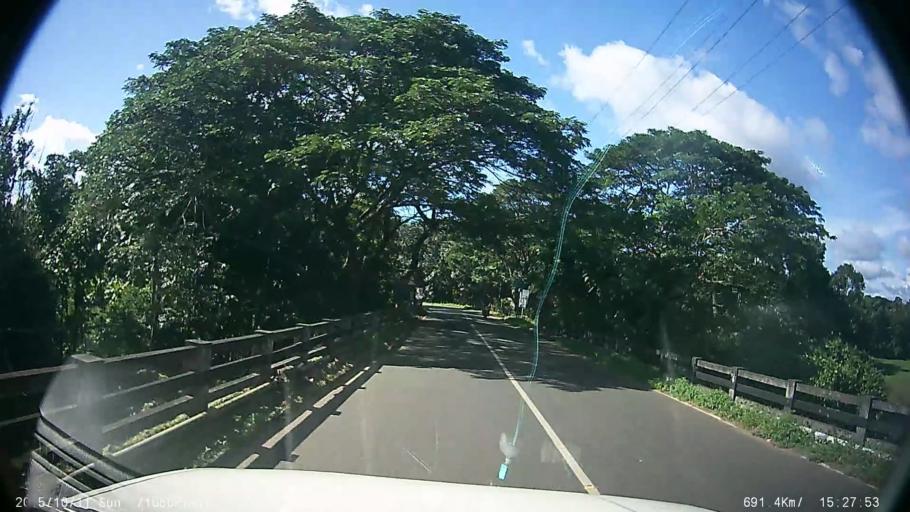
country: IN
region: Kerala
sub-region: Kottayam
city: Changanacheri
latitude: 9.4837
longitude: 76.5735
